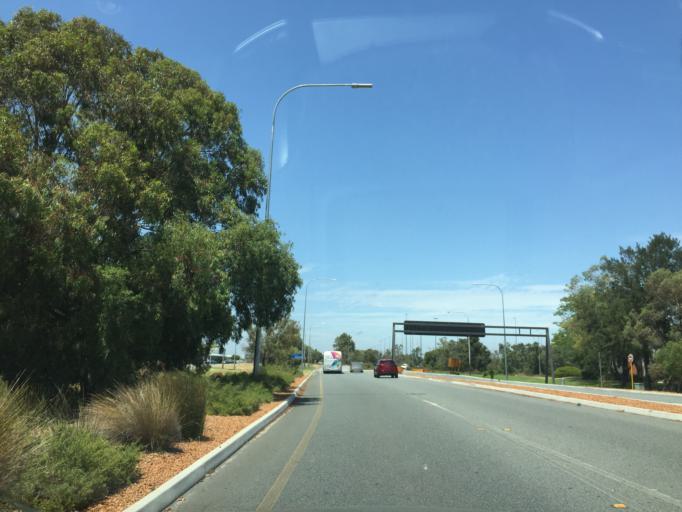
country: AU
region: Western Australia
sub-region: Belmont
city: Redcliffe
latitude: -31.9462
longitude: 115.9743
